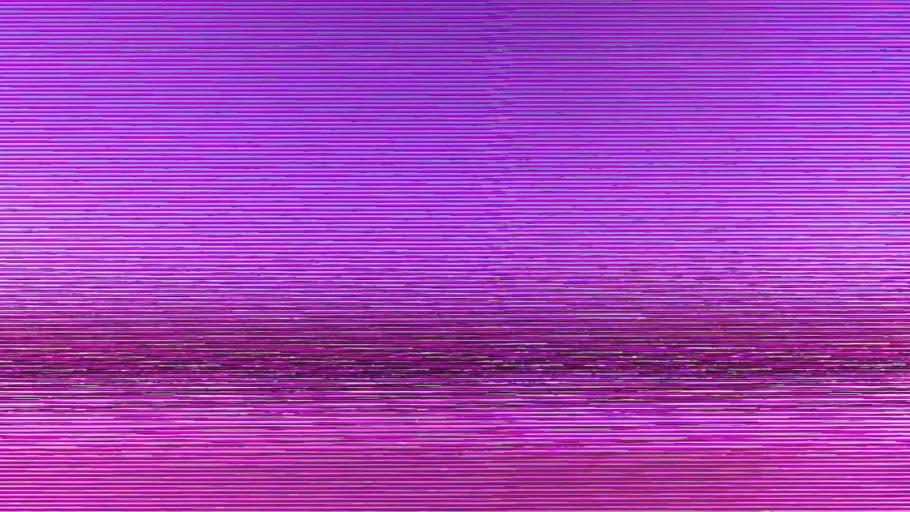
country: US
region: Michigan
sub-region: Oakland County
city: Farmington
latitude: 42.4638
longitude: -83.3568
